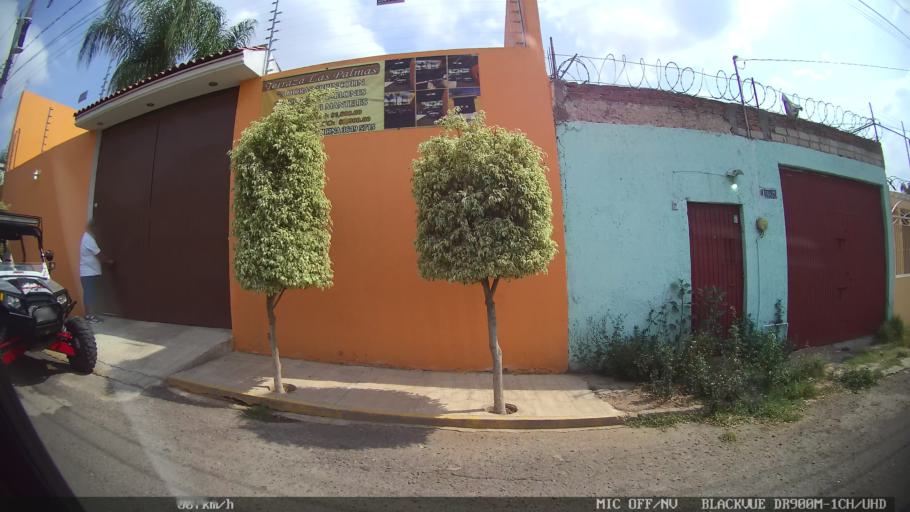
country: MX
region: Jalisco
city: Coyula
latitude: 20.6387
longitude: -103.2164
